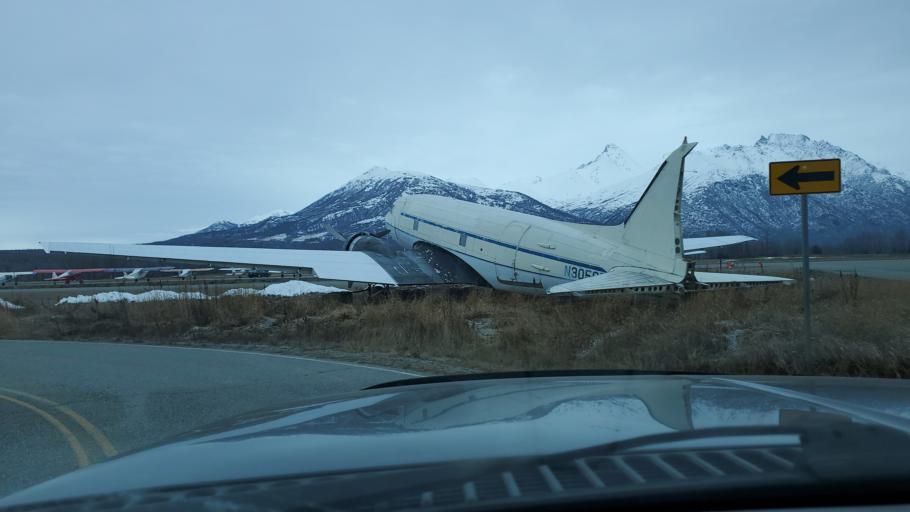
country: US
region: Alaska
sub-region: Matanuska-Susitna Borough
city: Palmer
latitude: 61.5980
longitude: -149.0940
